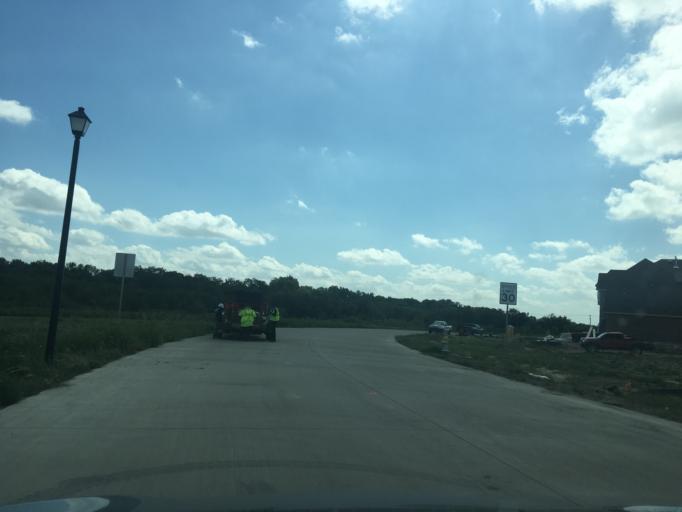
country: US
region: Texas
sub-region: Dallas County
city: Sachse
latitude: 32.9688
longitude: -96.5546
